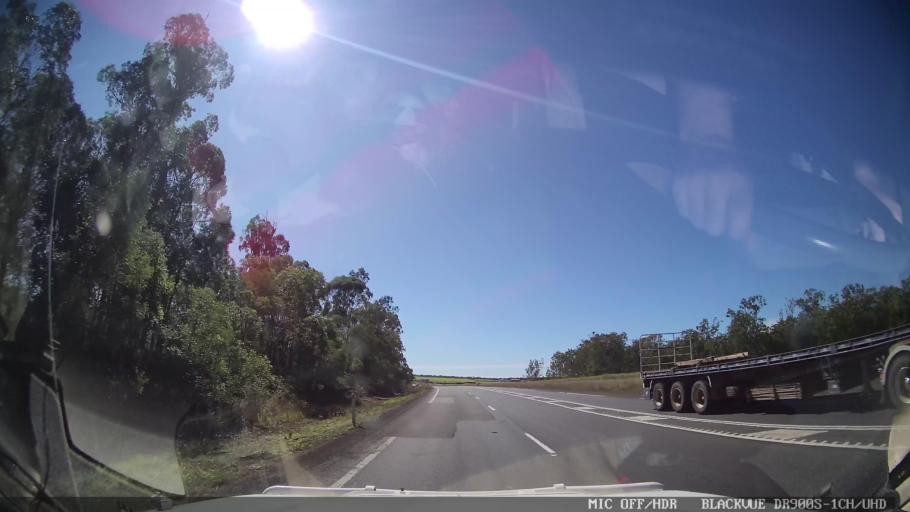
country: AU
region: Queensland
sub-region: Fraser Coast
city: Maryborough
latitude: -25.6475
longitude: 152.6361
